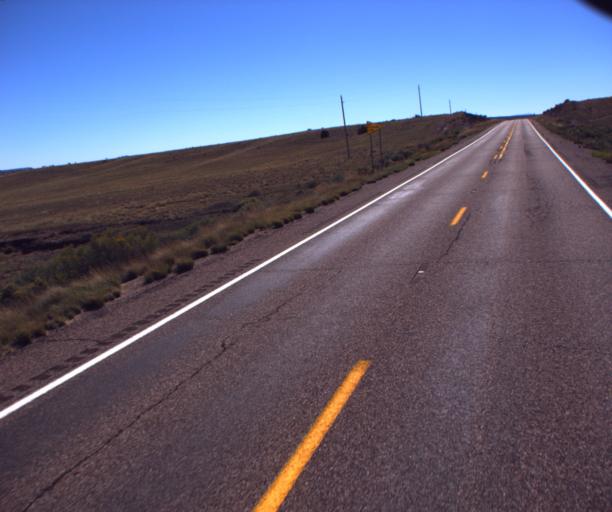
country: US
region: Arizona
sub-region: Apache County
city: Saint Johns
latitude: 34.5231
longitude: -109.4547
